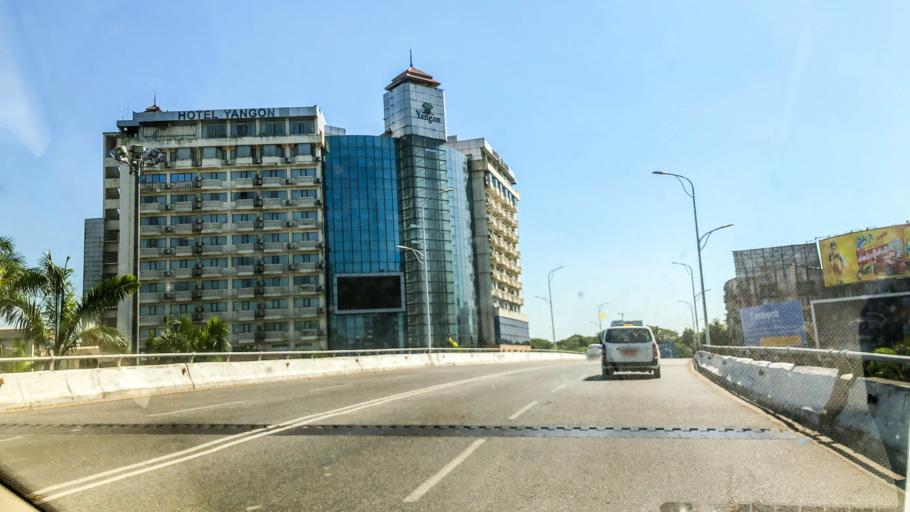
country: MM
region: Yangon
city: Yangon
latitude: 16.8669
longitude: 96.1421
